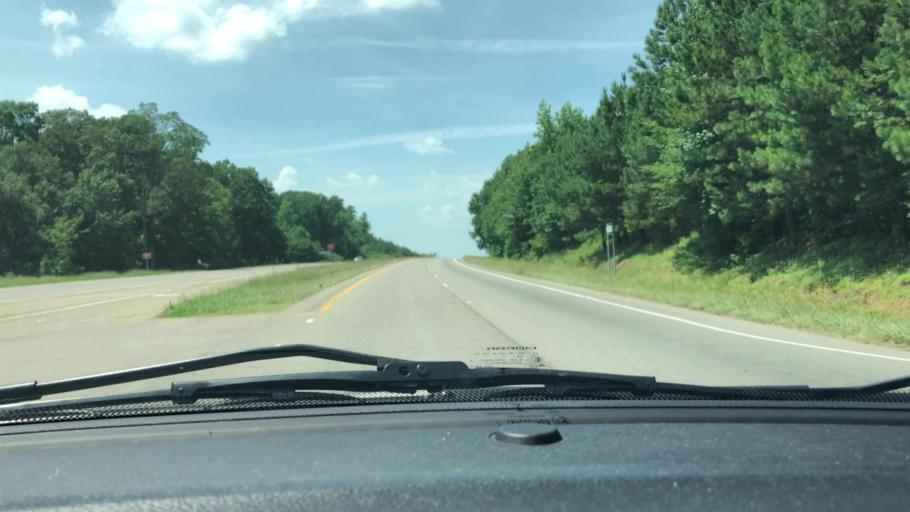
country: US
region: North Carolina
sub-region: Chatham County
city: Siler City
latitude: 35.6258
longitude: -79.3627
